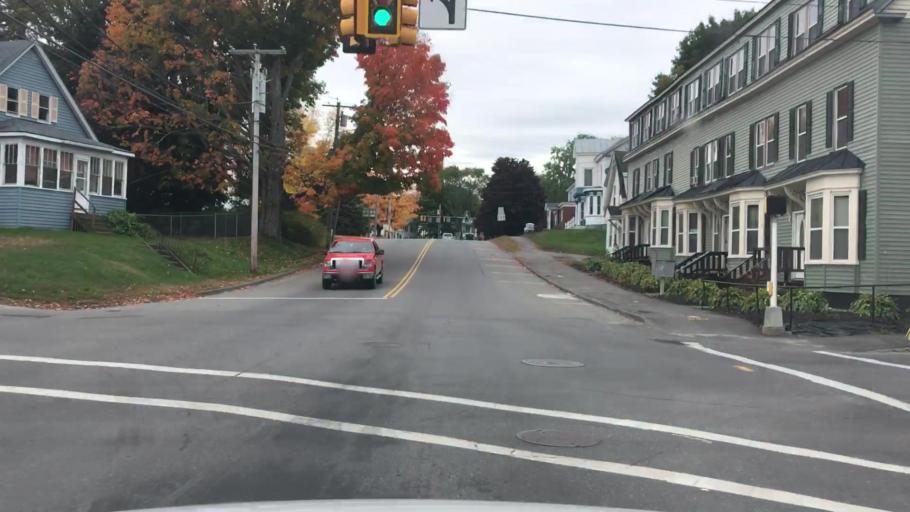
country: US
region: Maine
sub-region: Kennebec County
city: Waterville
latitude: 44.5475
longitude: -69.6351
